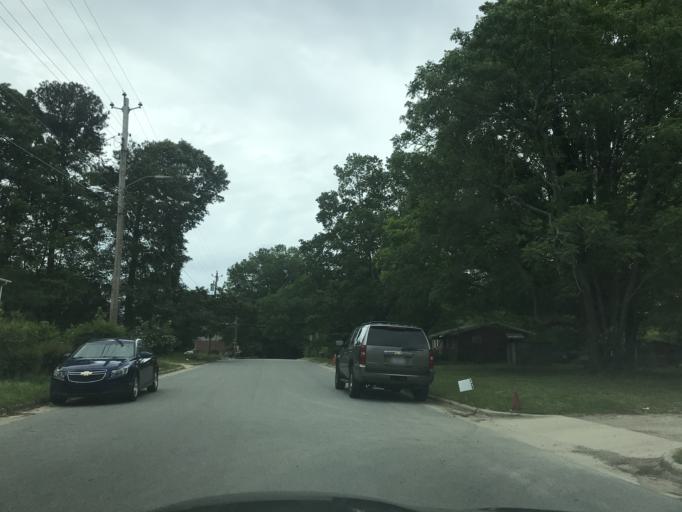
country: US
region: North Carolina
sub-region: Wake County
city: West Raleigh
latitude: 35.7907
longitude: -78.6905
